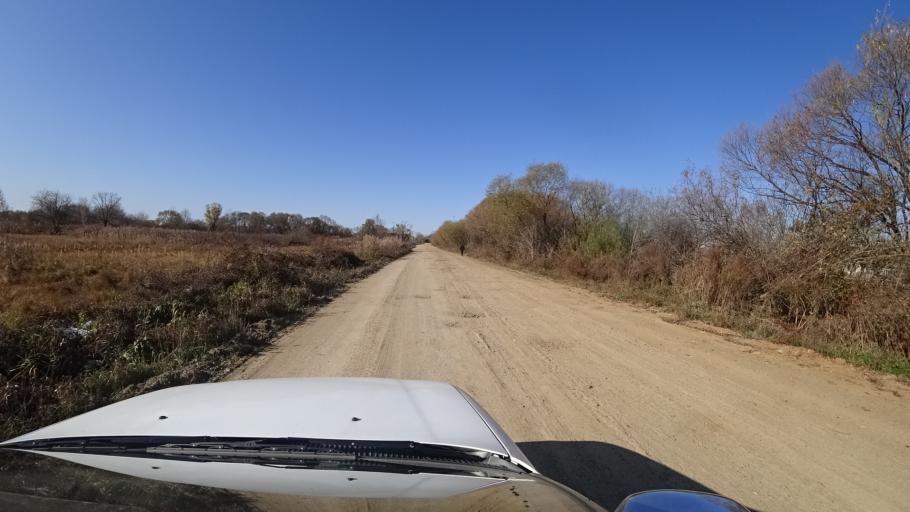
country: RU
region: Primorskiy
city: Dal'nerechensk
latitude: 45.9072
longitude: 133.8060
